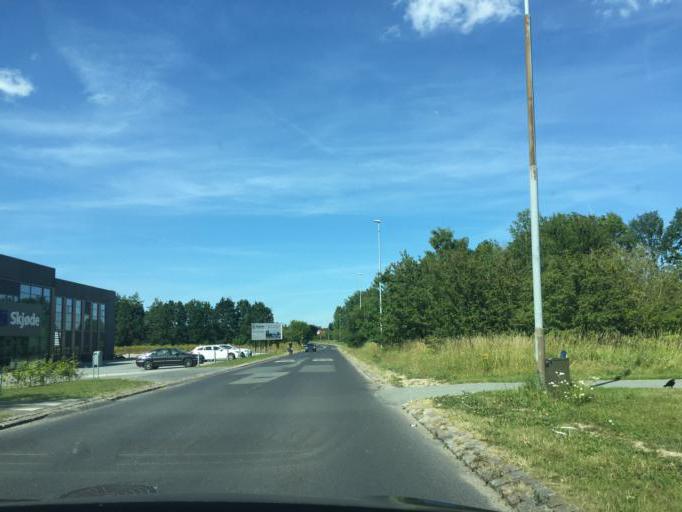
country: DK
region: South Denmark
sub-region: Odense Kommune
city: Neder Holluf
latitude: 55.3668
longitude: 10.4632
